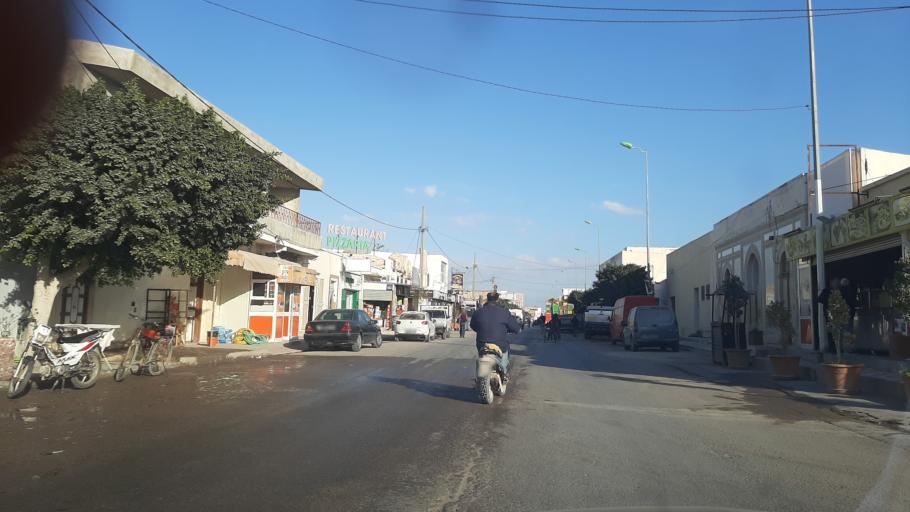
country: TN
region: Al Mahdiyah
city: El Jem
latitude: 35.2980
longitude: 10.7067
